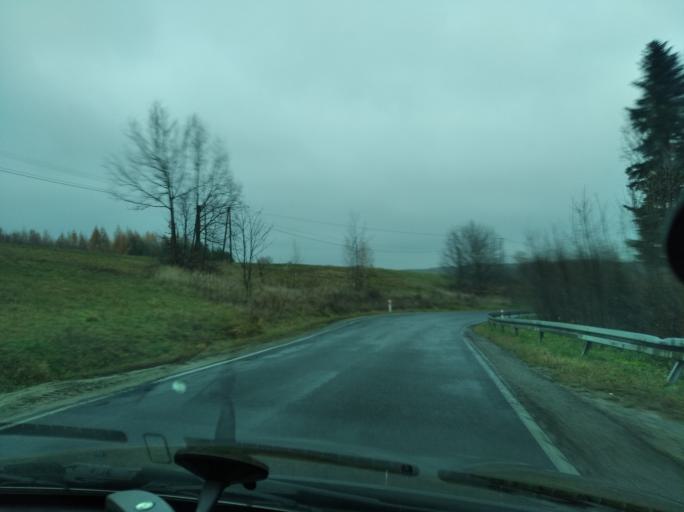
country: PL
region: Subcarpathian Voivodeship
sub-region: Powiat przeworski
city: Jawornik Polski
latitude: 49.8857
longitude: 22.2574
